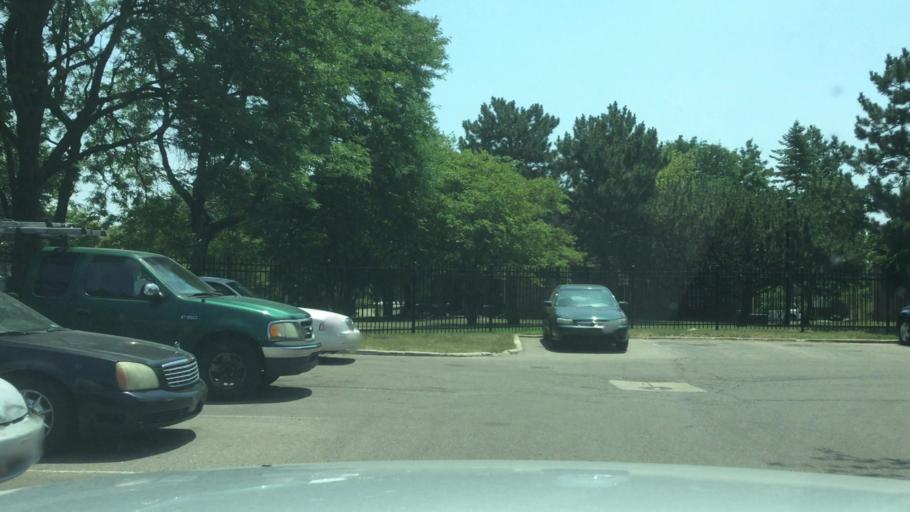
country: US
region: Michigan
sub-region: Wayne County
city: Detroit
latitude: 42.3453
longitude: -83.0215
